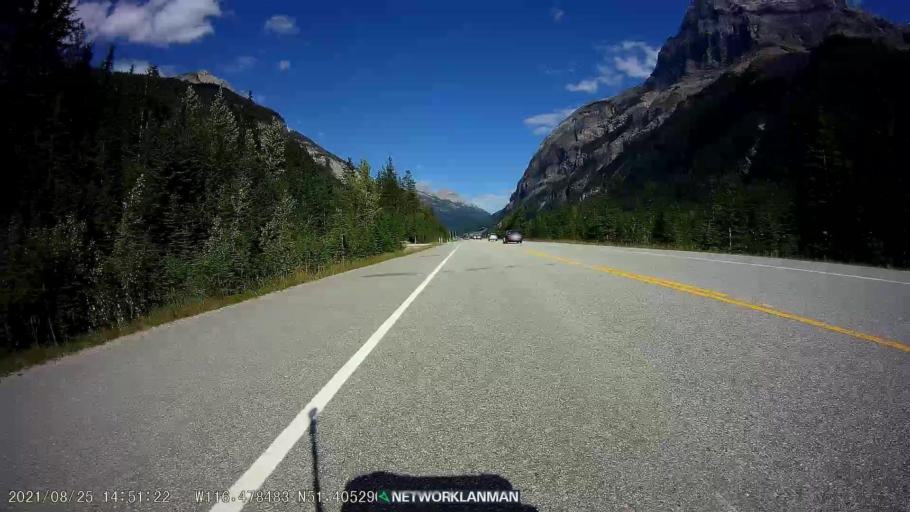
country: CA
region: Alberta
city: Lake Louise
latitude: 51.4054
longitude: -116.4788
